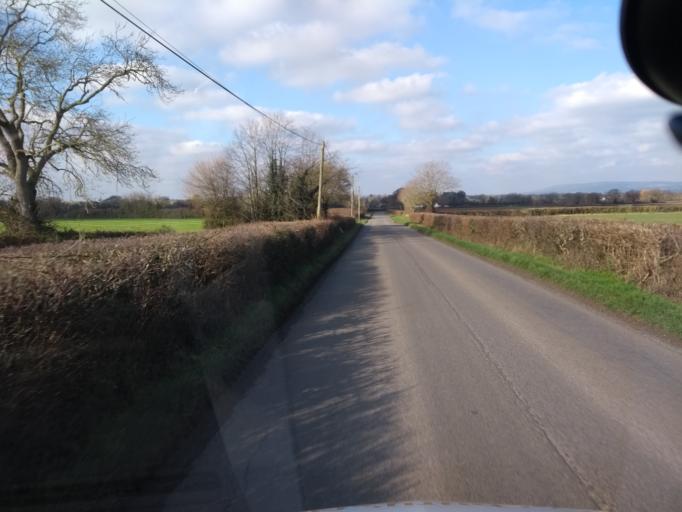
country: GB
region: England
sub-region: Somerset
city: Creech Saint Michael
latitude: 50.9840
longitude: -3.0621
